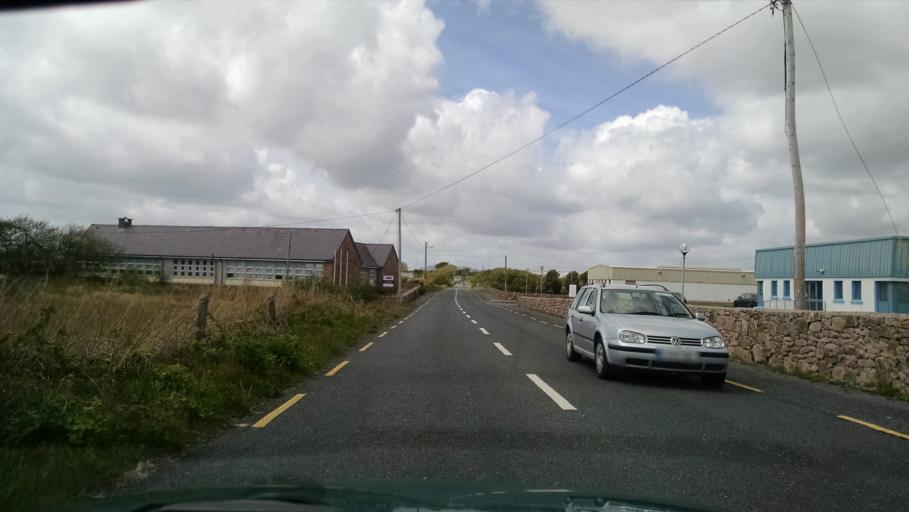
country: IE
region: Connaught
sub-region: County Galway
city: Clifden
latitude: 53.3207
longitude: -9.8110
